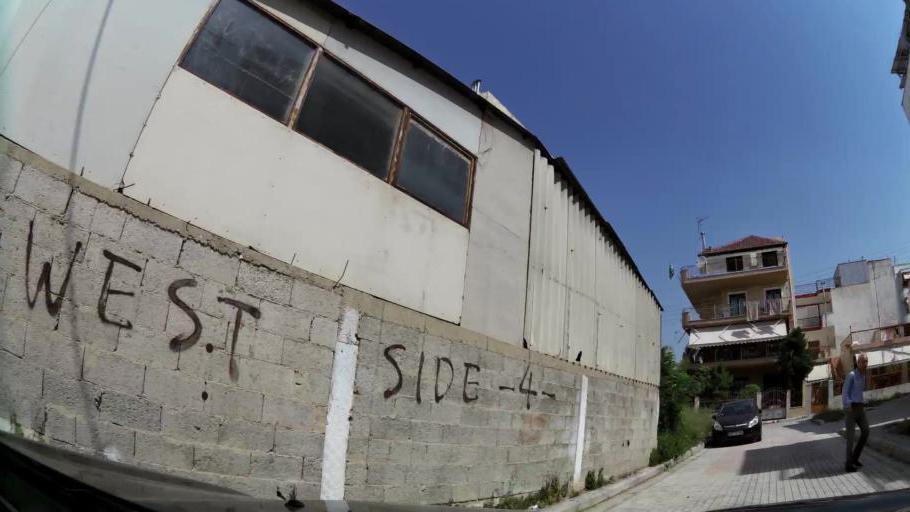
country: GR
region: Central Macedonia
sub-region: Nomos Thessalonikis
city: Evosmos
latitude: 40.6687
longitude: 22.9216
